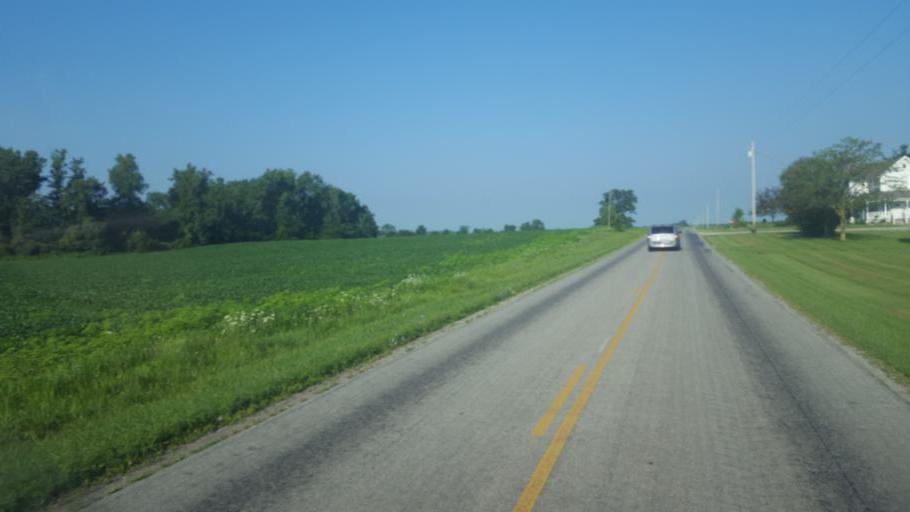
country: US
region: Ohio
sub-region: Hardin County
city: Kenton
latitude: 40.5388
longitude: -83.4730
